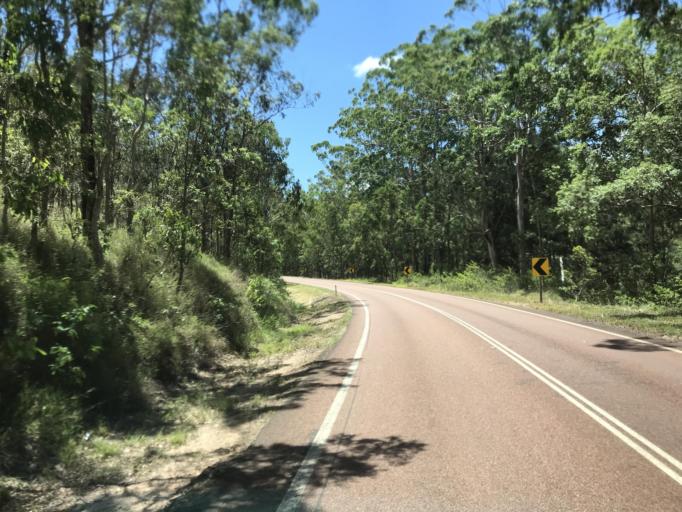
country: AU
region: Queensland
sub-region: Tablelands
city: Ravenshoe
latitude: -17.5894
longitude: 145.4726
